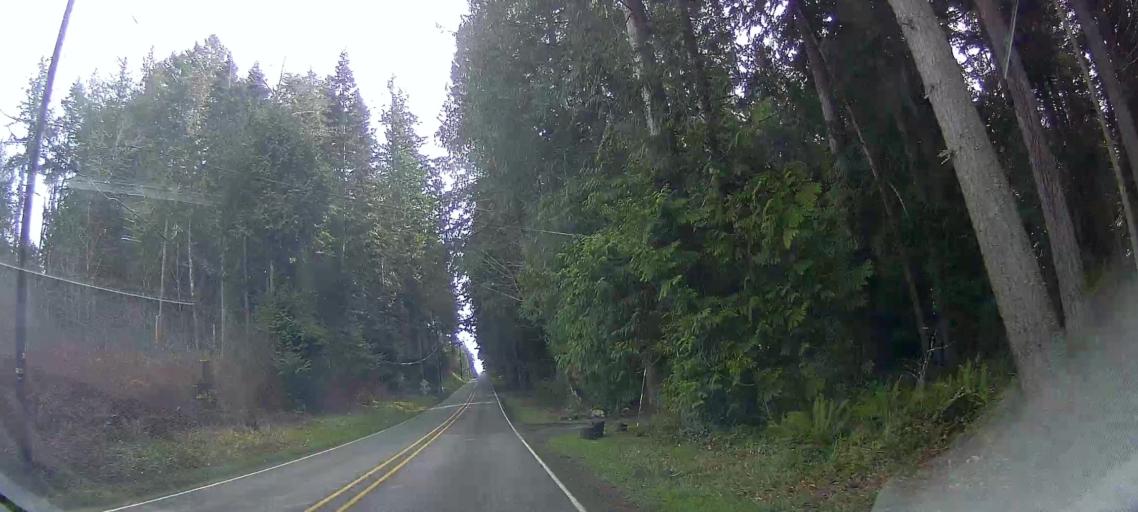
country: US
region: Washington
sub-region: Island County
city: Langley
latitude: 48.1037
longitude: -122.4190
